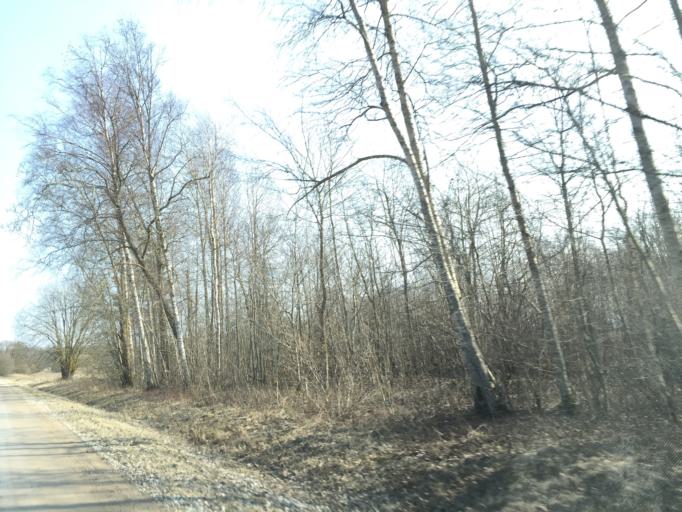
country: EE
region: Saare
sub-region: Kuressaare linn
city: Kuressaare
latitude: 58.3820
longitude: 22.6961
